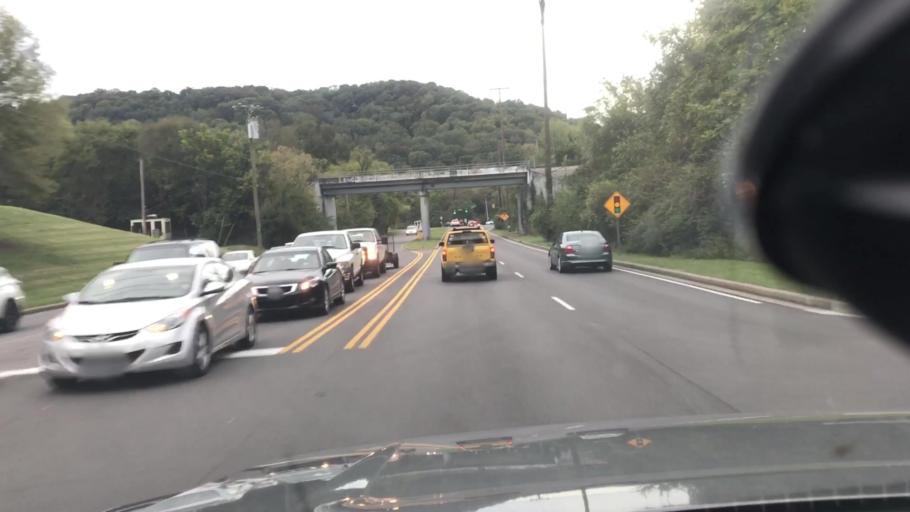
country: US
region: Tennessee
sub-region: Davidson County
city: Belle Meade
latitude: 36.0630
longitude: -86.9169
